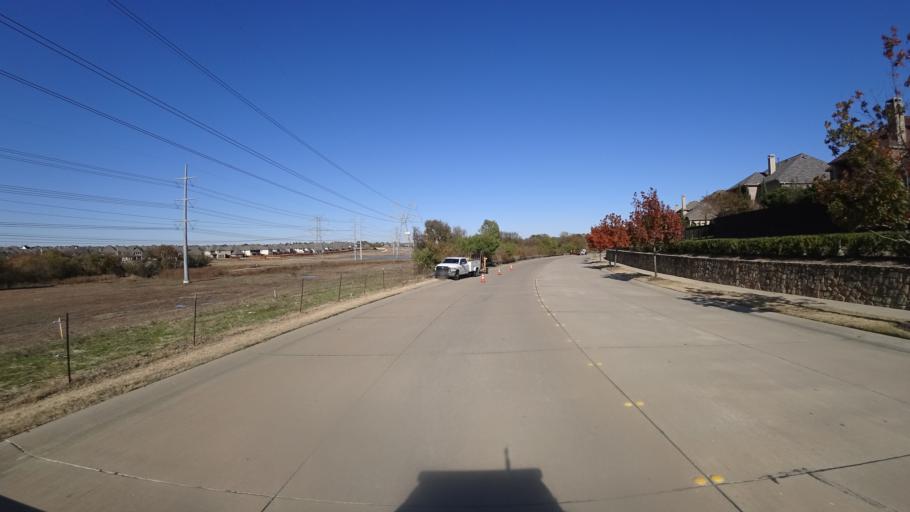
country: US
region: Texas
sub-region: Denton County
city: The Colony
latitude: 33.0291
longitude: -96.9137
